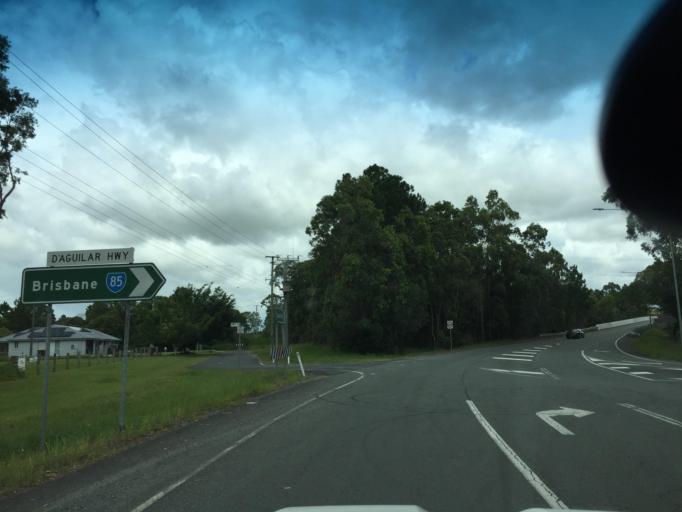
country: AU
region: Queensland
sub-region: Moreton Bay
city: Caboolture
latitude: -27.0596
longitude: 152.9102
